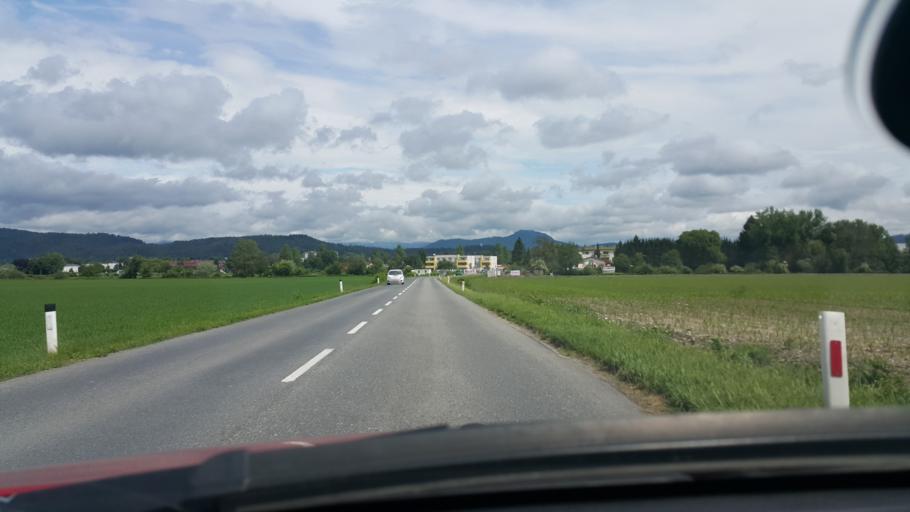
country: AT
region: Carinthia
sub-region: Klagenfurt am Woerthersee
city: Klagenfurt am Woerthersee
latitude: 46.6005
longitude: 14.2899
